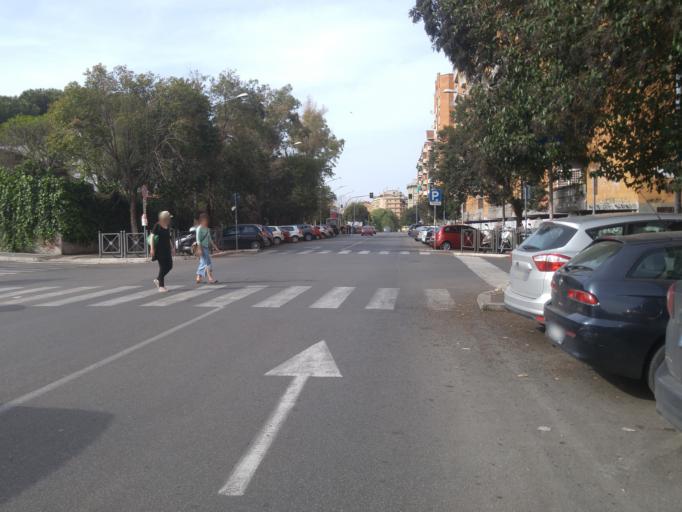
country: IT
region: Latium
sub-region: Citta metropolitana di Roma Capitale
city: Rome
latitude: 41.8657
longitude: 12.4844
